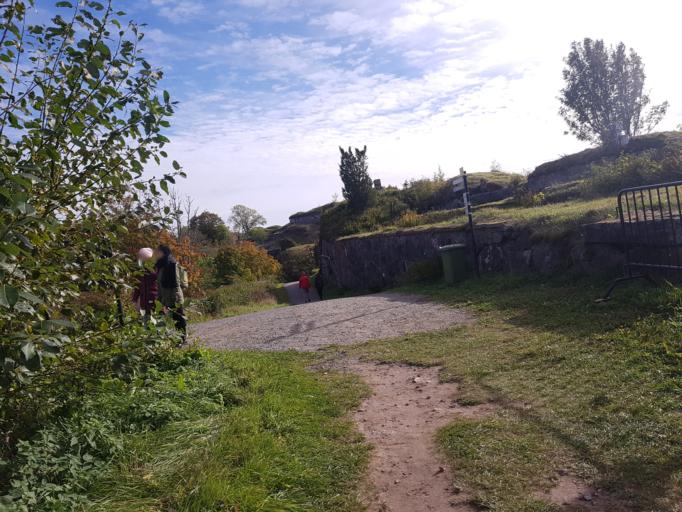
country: FI
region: Uusimaa
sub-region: Helsinki
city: Helsinki
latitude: 60.1362
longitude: 24.9963
